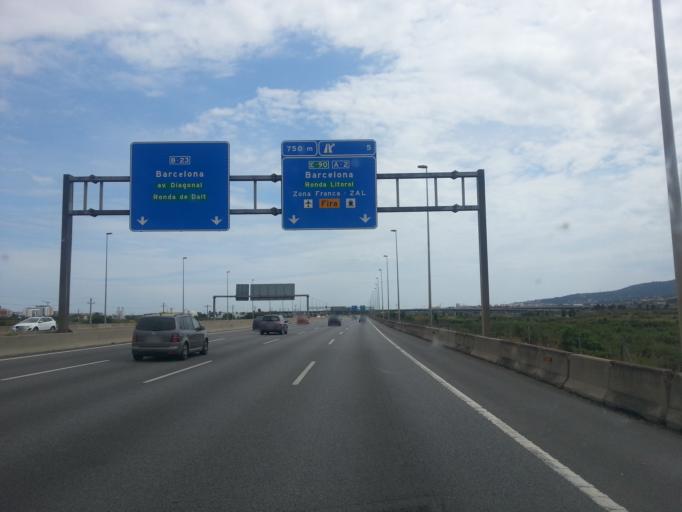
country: ES
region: Catalonia
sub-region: Provincia de Barcelona
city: Sant Vicenc dels Horts
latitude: 41.3876
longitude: 2.0271
